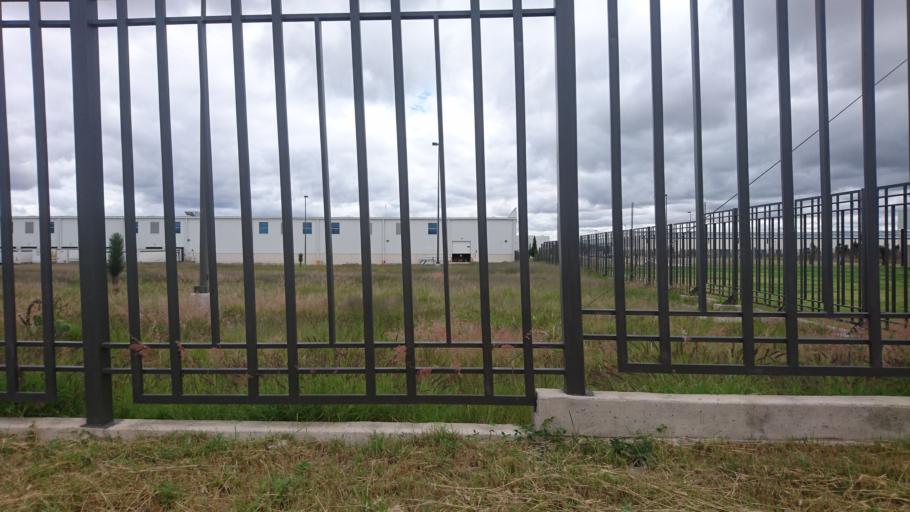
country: MX
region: San Luis Potosi
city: La Pila
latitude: 21.9840
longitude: -100.8695
